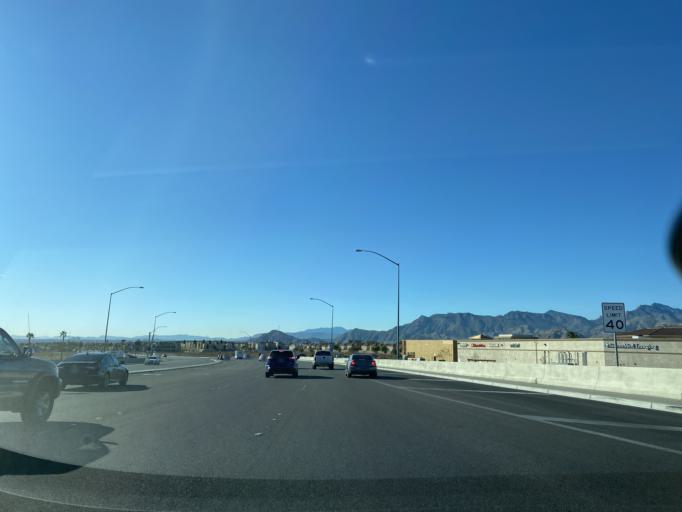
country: US
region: Nevada
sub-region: Clark County
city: Summerlin South
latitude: 36.2970
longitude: -115.2874
